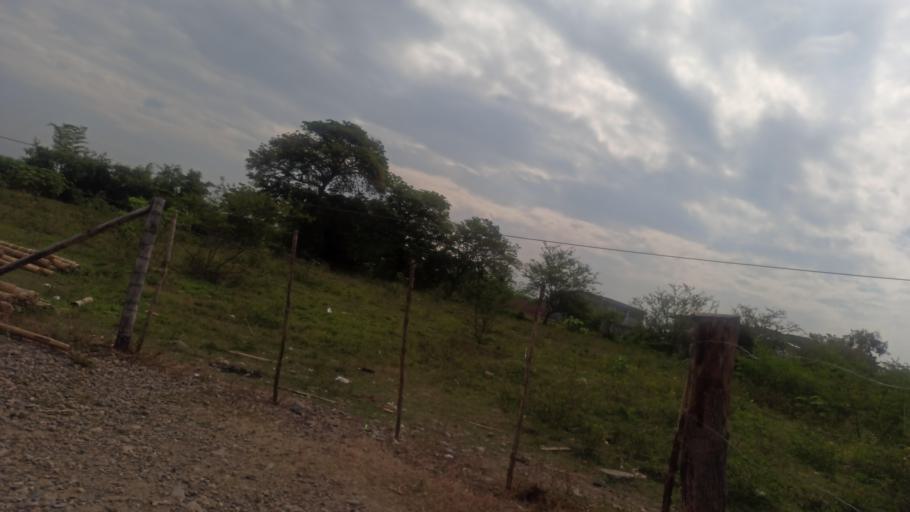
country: CO
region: Valle del Cauca
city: Jamundi
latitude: 3.1301
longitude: -76.5574
